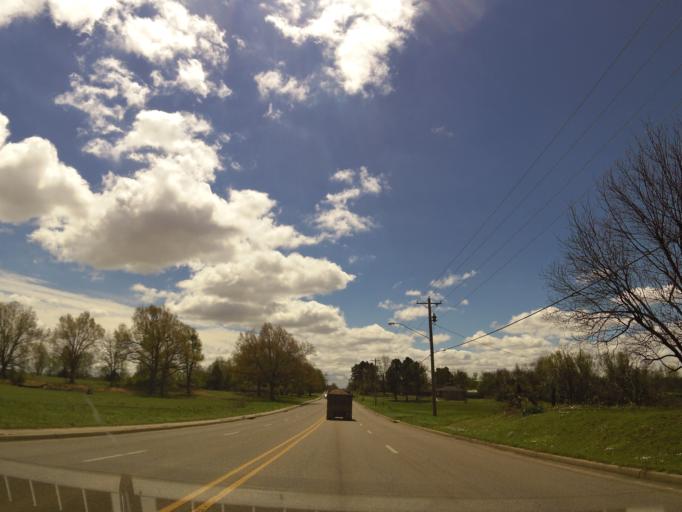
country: US
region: Arkansas
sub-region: Craighead County
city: Jonesboro
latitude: 35.8718
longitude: -90.7029
